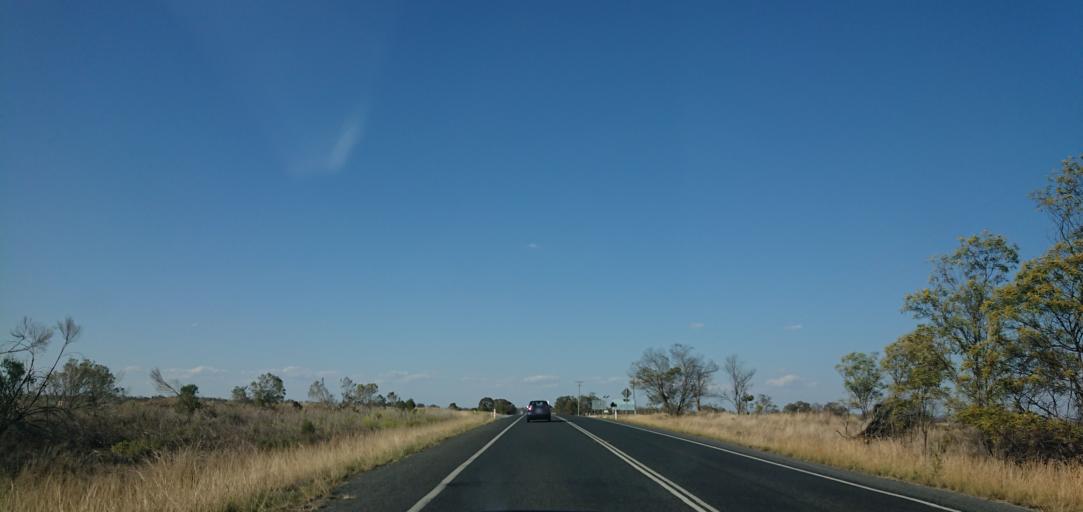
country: AU
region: Queensland
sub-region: Toowoomba
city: Westbrook
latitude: -27.6444
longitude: 151.7321
